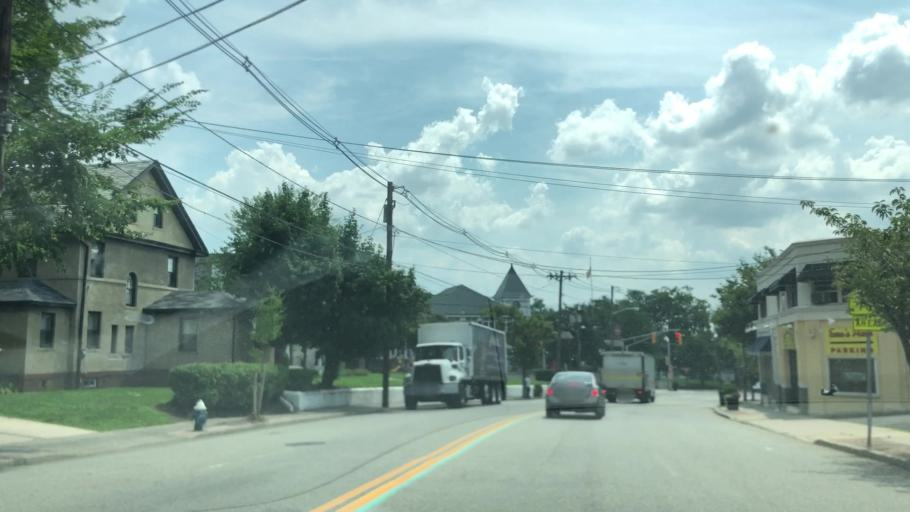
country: US
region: New Jersey
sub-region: Essex County
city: West Orange
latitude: 40.7889
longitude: -74.2315
